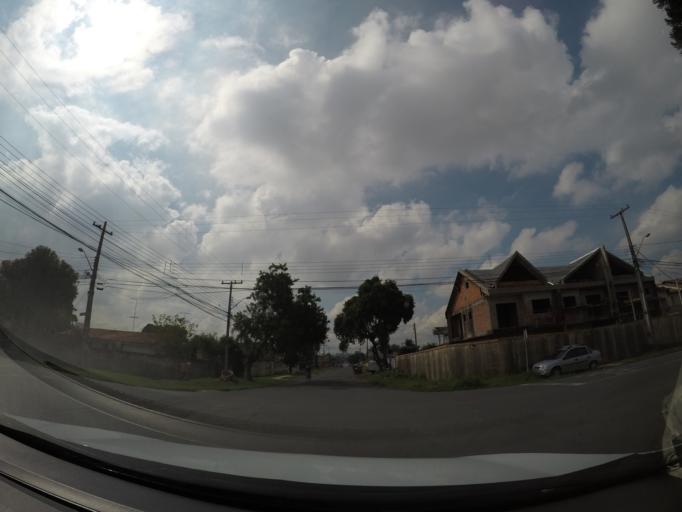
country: BR
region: Parana
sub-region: Sao Jose Dos Pinhais
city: Sao Jose dos Pinhais
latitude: -25.4875
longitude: -49.2528
